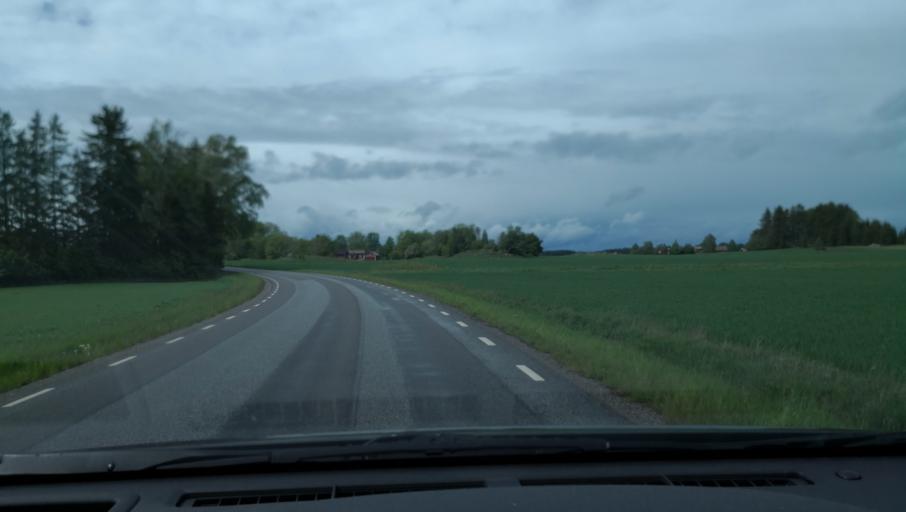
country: SE
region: Uppsala
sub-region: Enkopings Kommun
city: Orsundsbro
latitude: 59.6983
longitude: 17.3670
